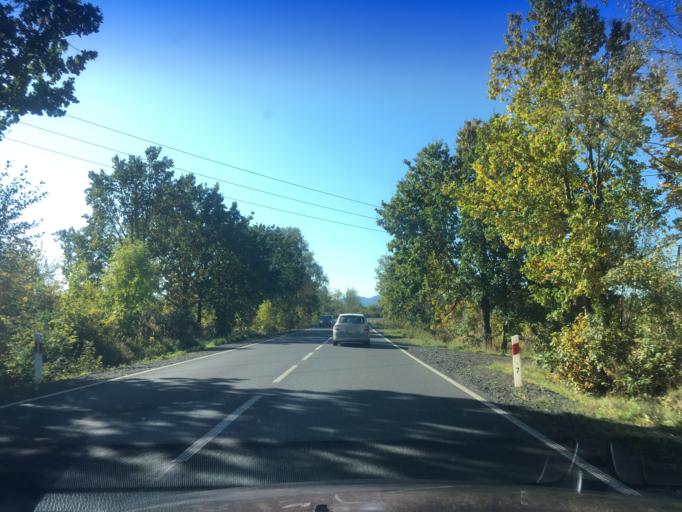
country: DE
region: Saxony
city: Hirschfelde
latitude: 50.9175
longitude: 14.8693
